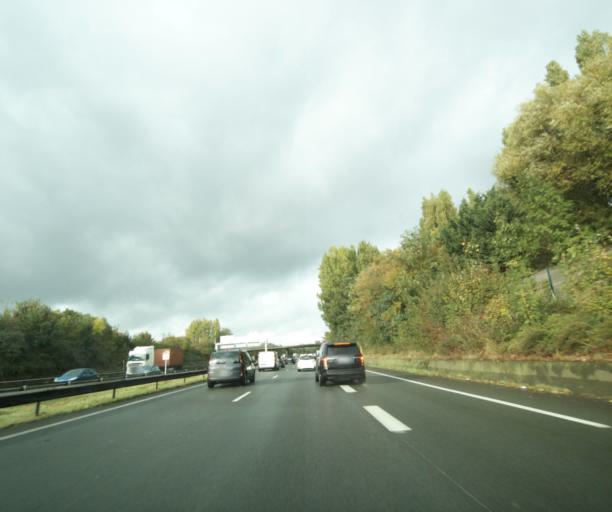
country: FR
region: Nord-Pas-de-Calais
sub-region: Departement du Nord
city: Bondues
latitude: 50.6869
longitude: 3.1114
